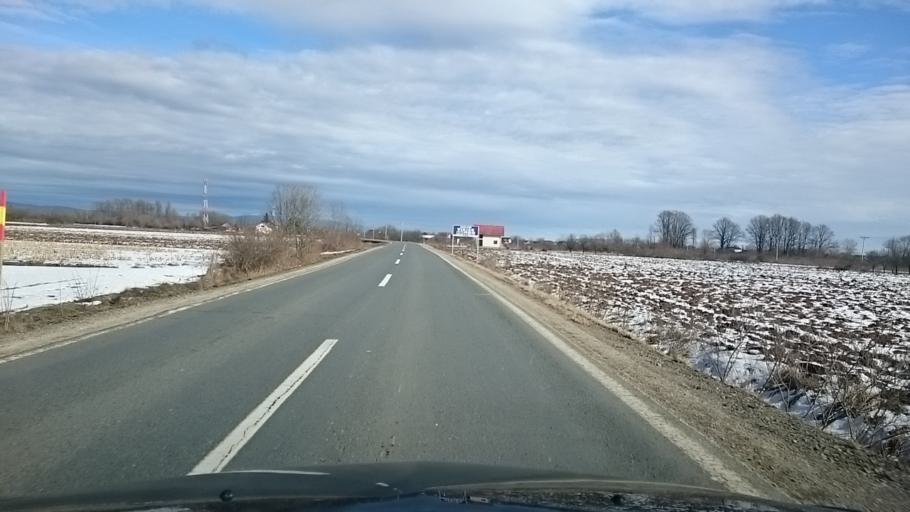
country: BA
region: Republika Srpska
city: Bosanska Dubica
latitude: 45.2106
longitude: 16.9369
